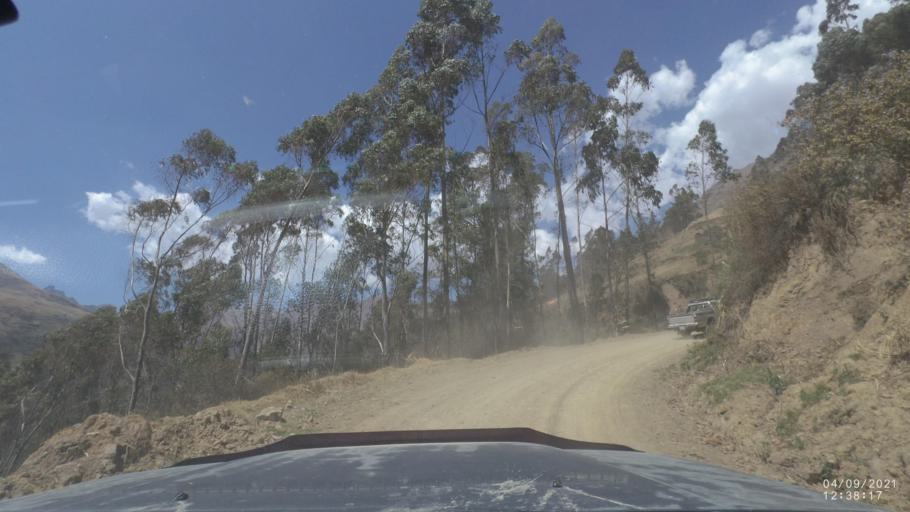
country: BO
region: Cochabamba
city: Colchani
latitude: -17.2277
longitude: -66.5021
